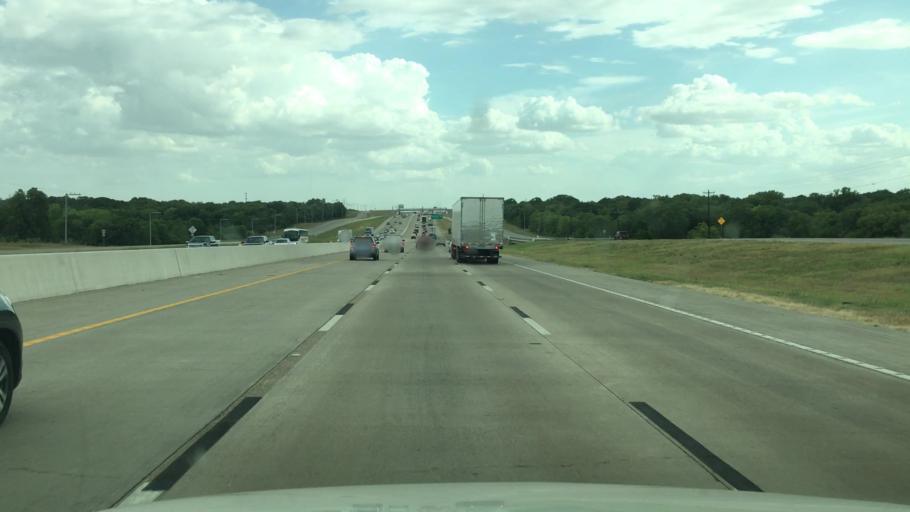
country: US
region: Texas
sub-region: McLennan County
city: Lorena
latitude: 31.3723
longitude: -97.2155
